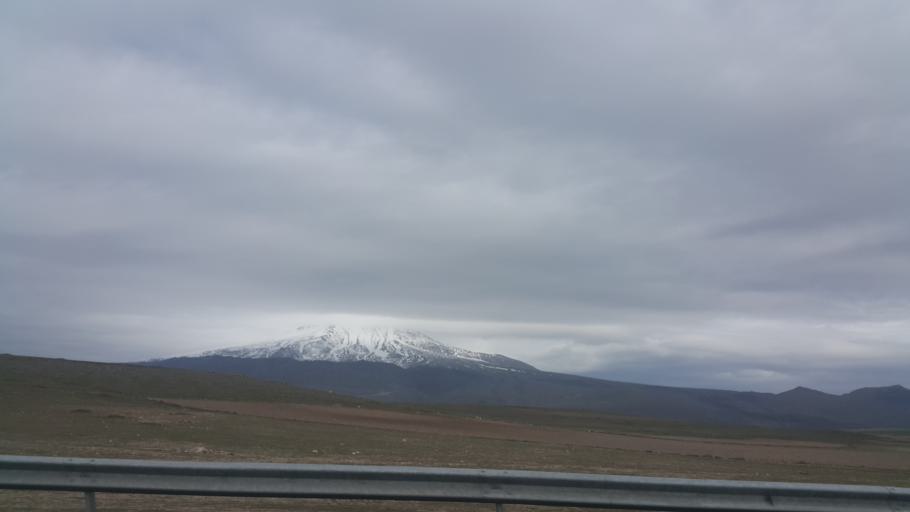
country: TR
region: Aksaray
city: Taspinar
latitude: 38.1160
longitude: 34.0339
